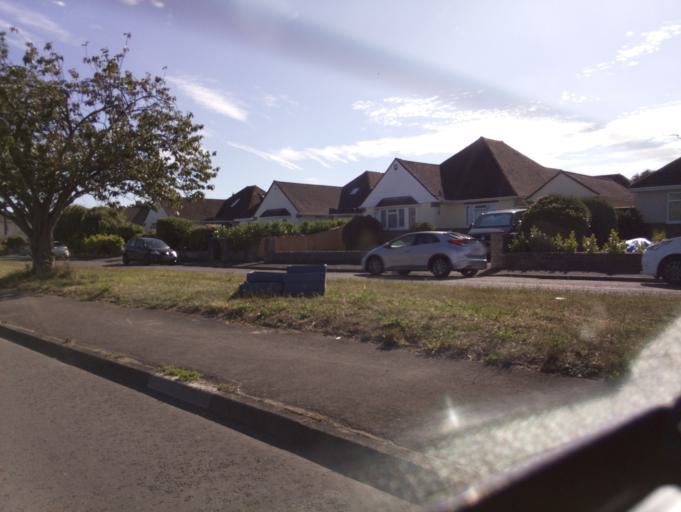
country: GB
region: England
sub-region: Dorset
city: Ferndown
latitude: 50.7786
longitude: -1.8821
